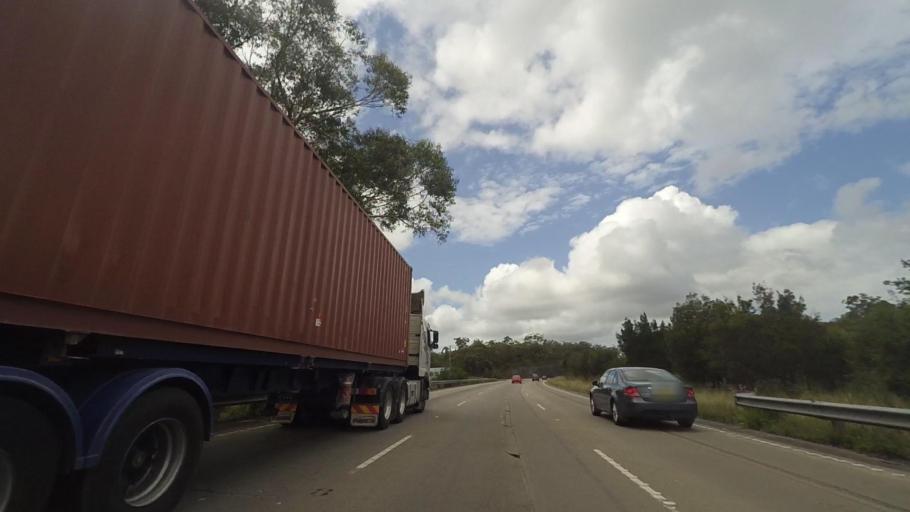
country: AU
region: New South Wales
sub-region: Gosford Shire
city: Point Clare
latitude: -33.4264
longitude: 151.2281
